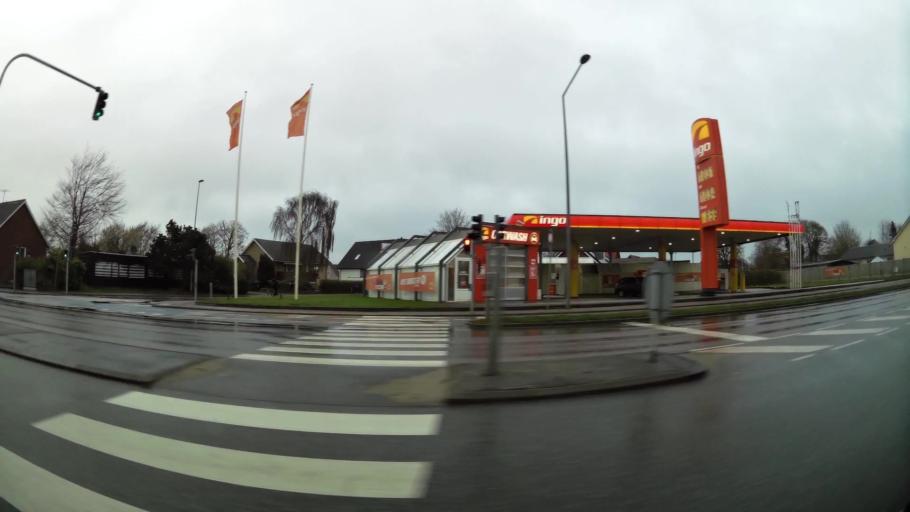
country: DK
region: Central Jutland
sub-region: Herning Kommune
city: Herning
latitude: 56.1373
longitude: 8.9478
